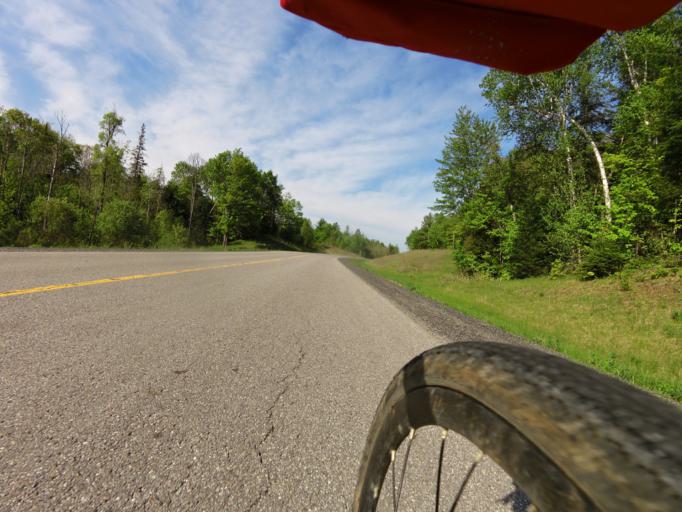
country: CA
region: Ontario
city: Arnprior
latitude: 45.1618
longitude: -76.5064
